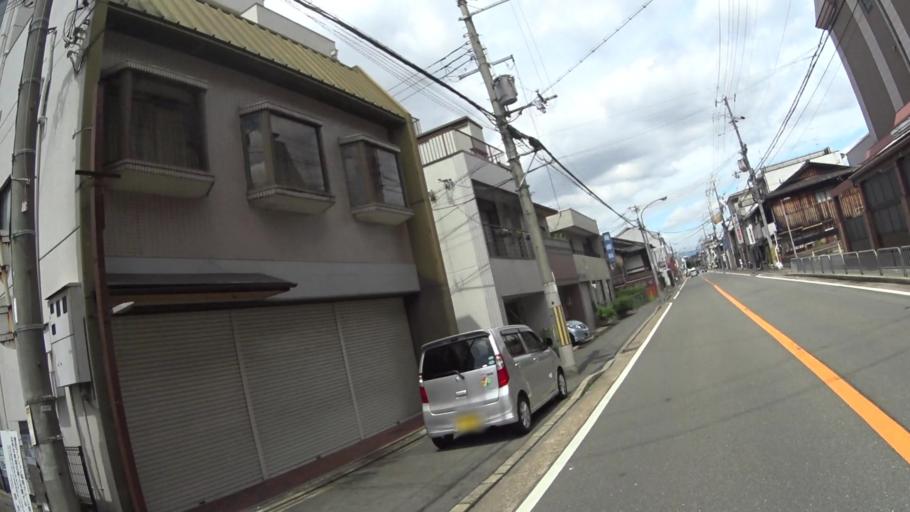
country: JP
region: Kyoto
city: Kyoto
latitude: 34.9696
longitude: 135.7685
